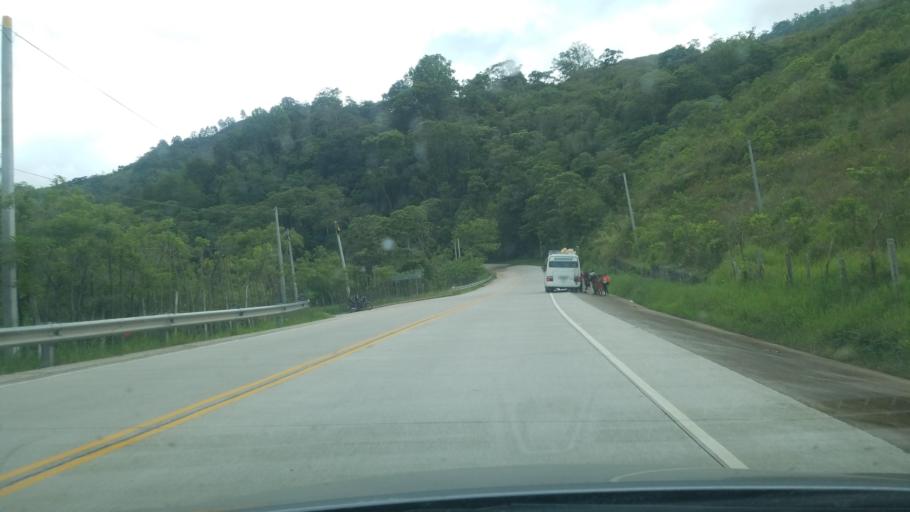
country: HN
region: Copan
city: San Jeronimo
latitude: 14.9288
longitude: -88.9380
